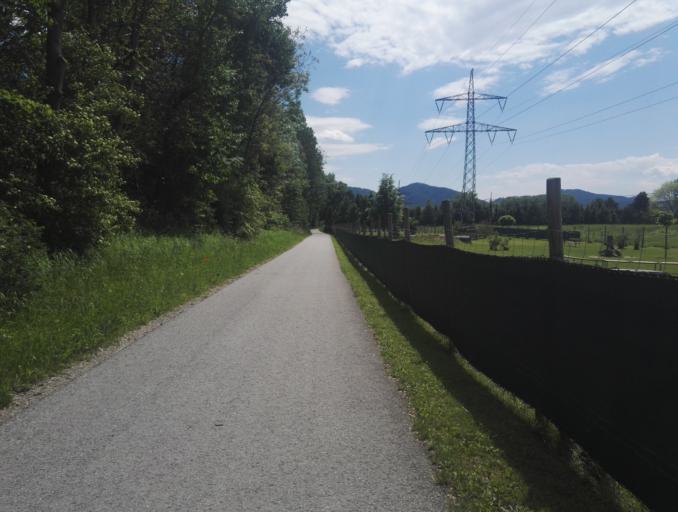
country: AT
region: Styria
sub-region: Politischer Bezirk Graz-Umgebung
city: Gratkorn
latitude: 47.1423
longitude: 15.3281
